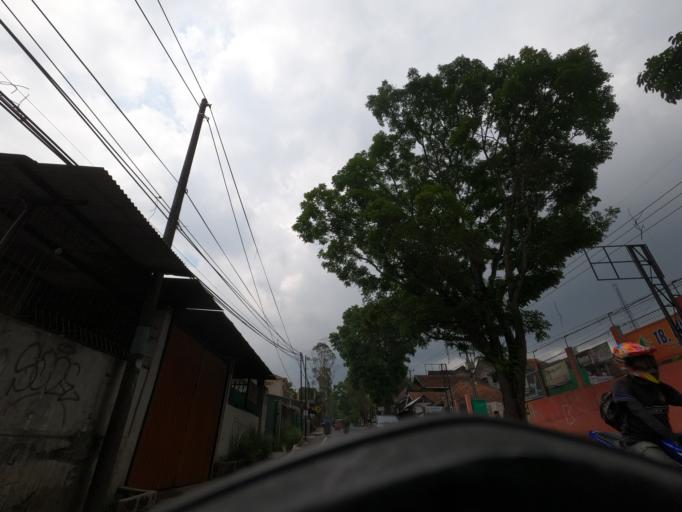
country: ID
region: West Java
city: Sukabumi
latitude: -6.7703
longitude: 107.0605
